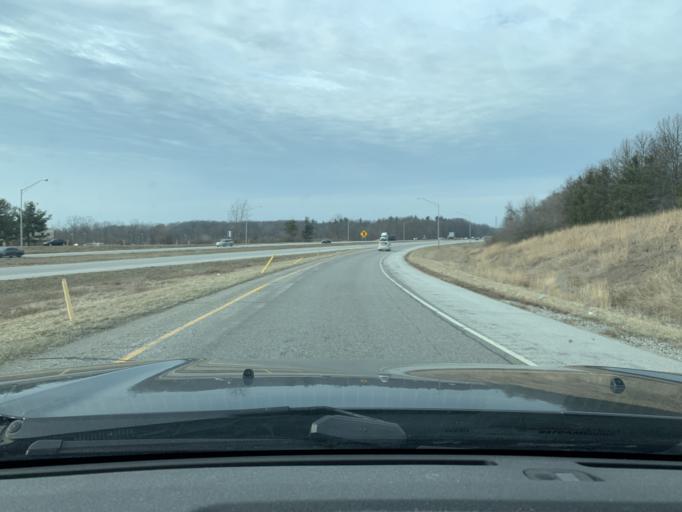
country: US
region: Indiana
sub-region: Porter County
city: Chesterton
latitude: 41.5521
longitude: -87.0458
